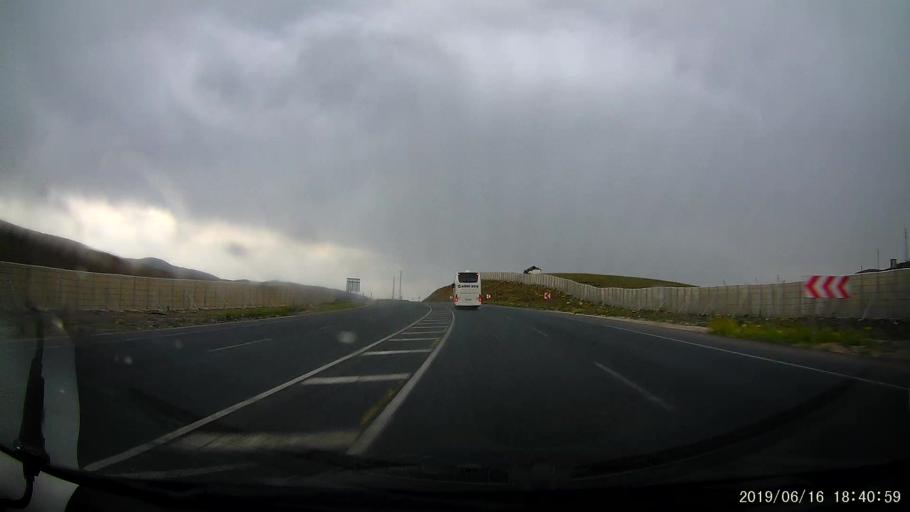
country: TR
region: Erzincan
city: Catalarmut
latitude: 39.8785
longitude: 39.1350
